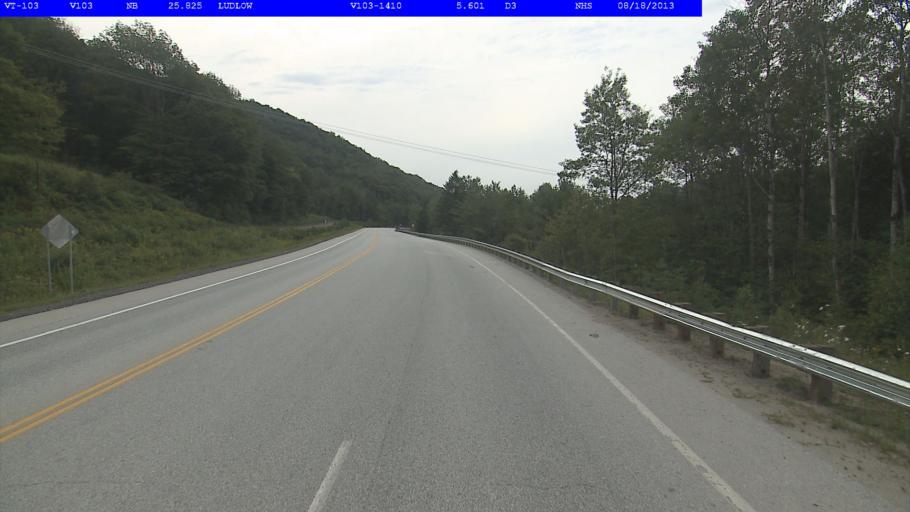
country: US
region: Vermont
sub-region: Windsor County
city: Chester
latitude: 43.4346
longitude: -72.7295
